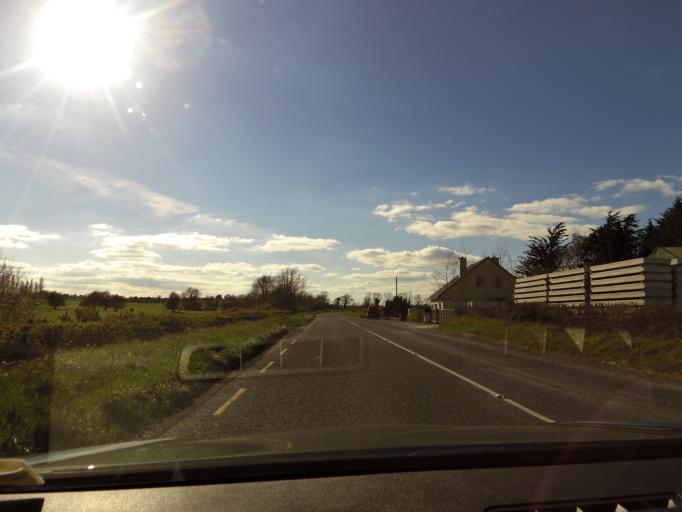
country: IE
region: Leinster
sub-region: Uibh Fhaili
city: Banagher
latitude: 53.1031
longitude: -8.0142
